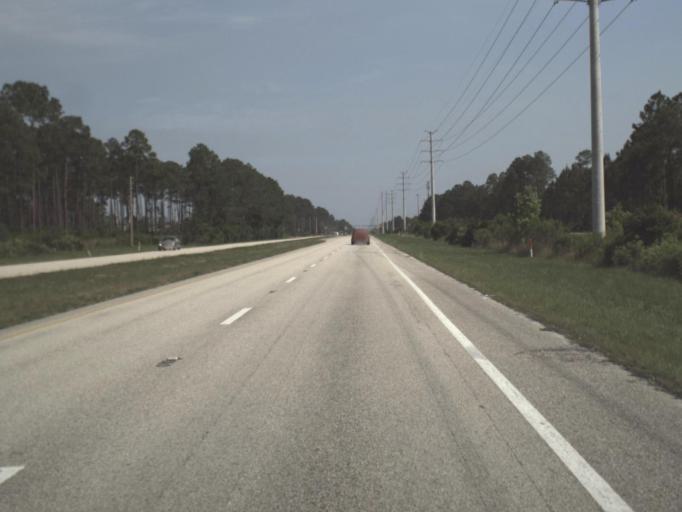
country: US
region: Florida
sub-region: Saint Johns County
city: Villano Beach
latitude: 30.0187
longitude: -81.3978
